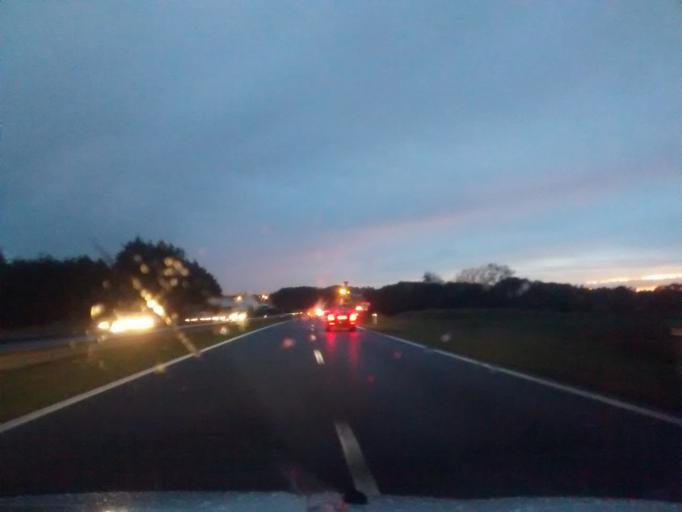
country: FR
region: Brittany
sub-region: Departement des Cotes-d'Armor
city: Tremuson
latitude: 48.5260
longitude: -2.8654
